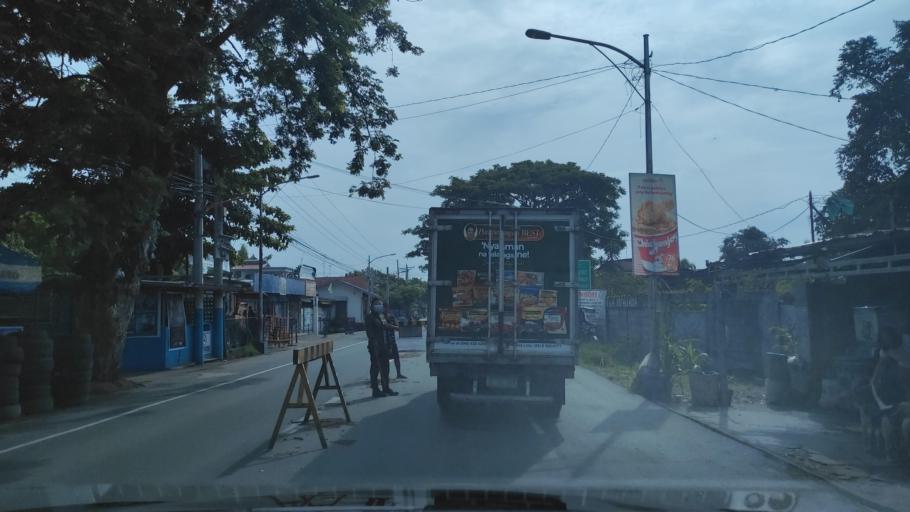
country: PH
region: Central Luzon
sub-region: Province of Nueva Ecija
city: San Vicente
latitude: 15.2101
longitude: 120.8144
